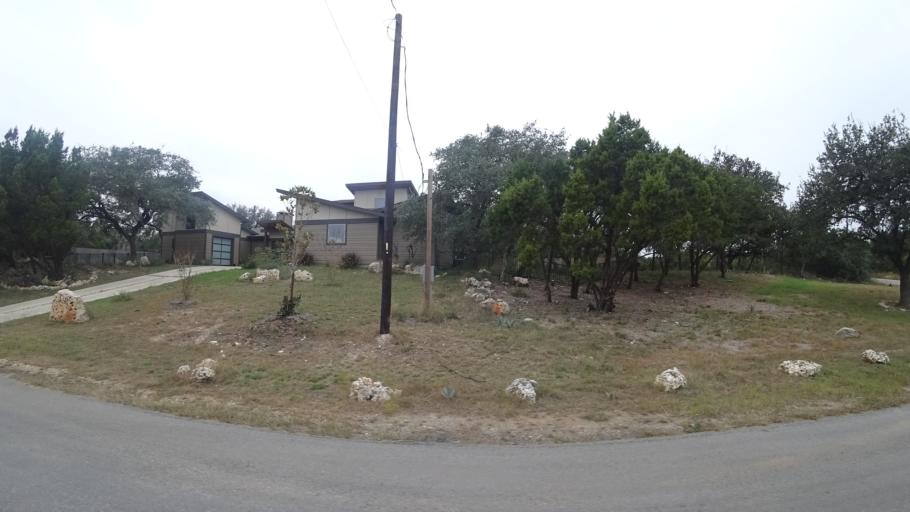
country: US
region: Texas
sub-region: Travis County
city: Hudson Bend
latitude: 30.3698
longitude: -97.9255
